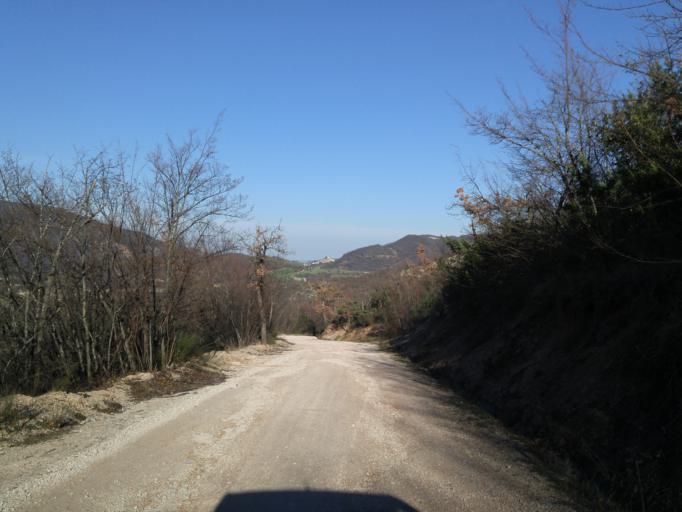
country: IT
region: The Marches
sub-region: Provincia di Pesaro e Urbino
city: Canavaccio
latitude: 43.6557
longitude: 12.7485
